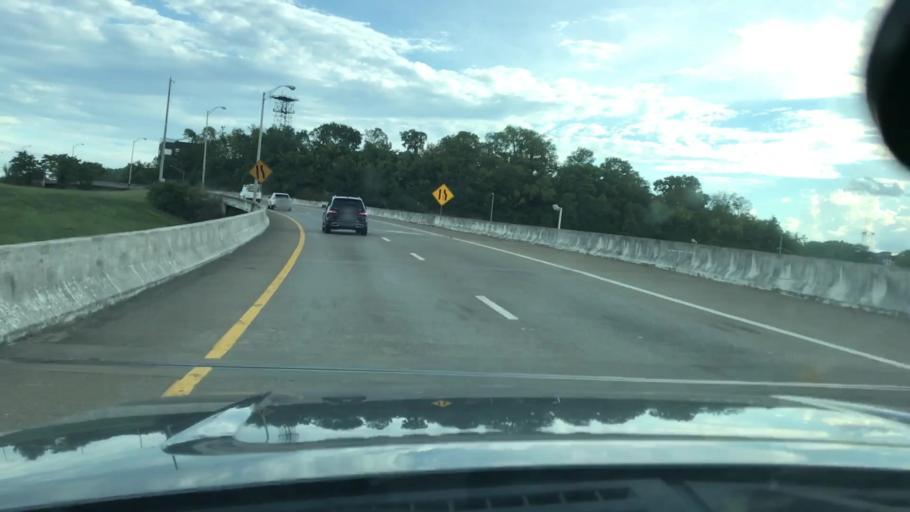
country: US
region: Tennessee
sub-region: Davidson County
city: Nashville
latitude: 36.1556
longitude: -86.8141
